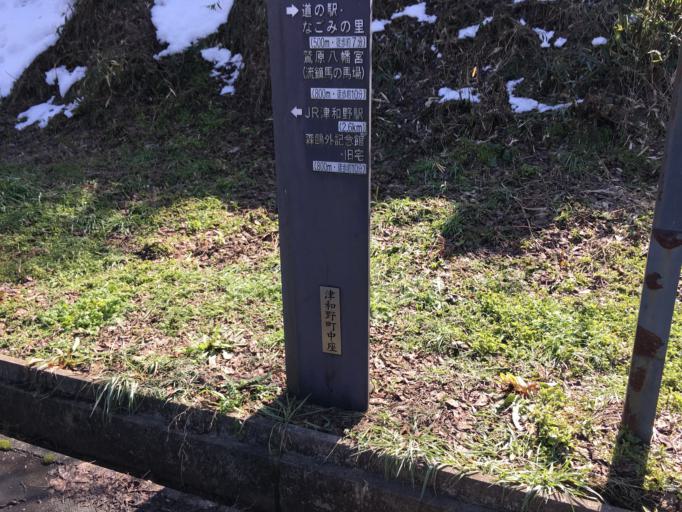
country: JP
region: Shimane
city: Masuda
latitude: 34.4514
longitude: 131.7652
